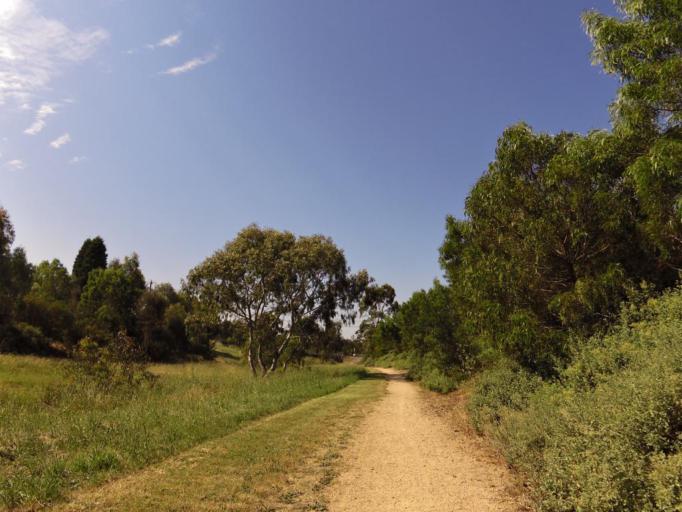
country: AU
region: Victoria
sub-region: Whittlesea
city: Epping
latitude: -37.6395
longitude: 145.0337
